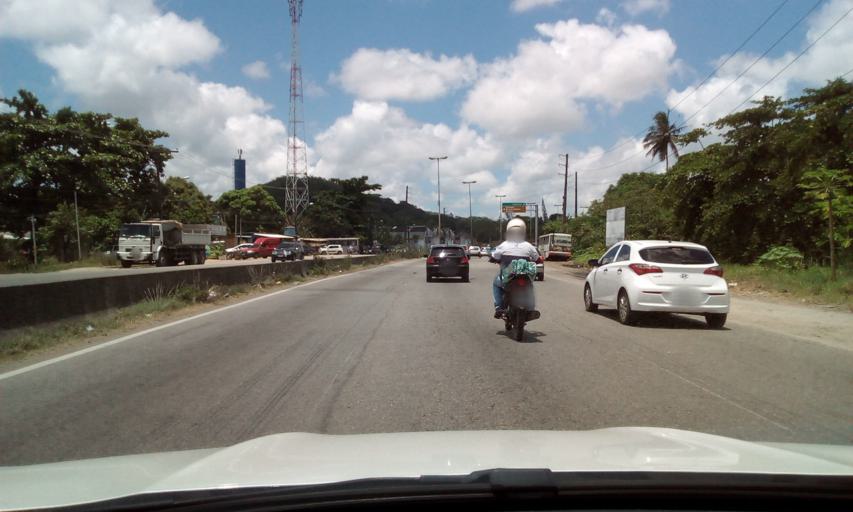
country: BR
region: Pernambuco
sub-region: Recife
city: Recife
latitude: -8.0203
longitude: -34.9426
